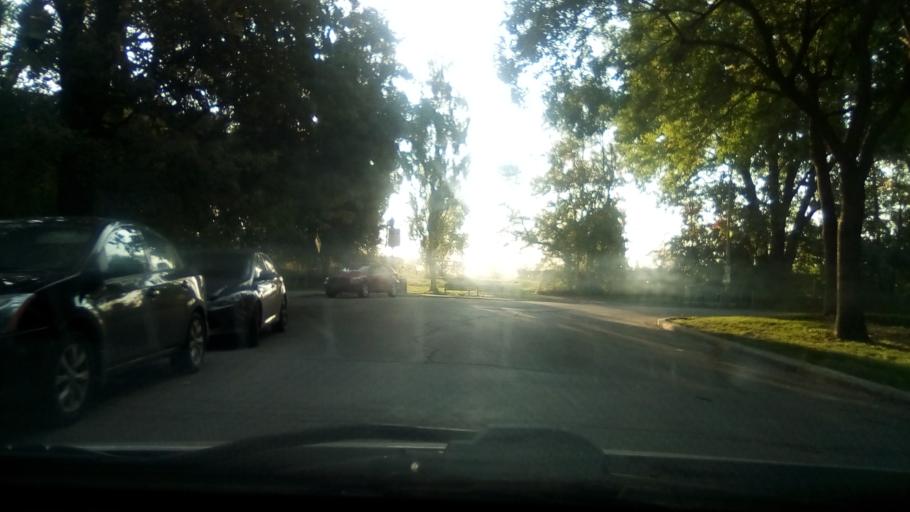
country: CA
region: Quebec
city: Westmount
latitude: 45.4755
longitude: -73.5572
